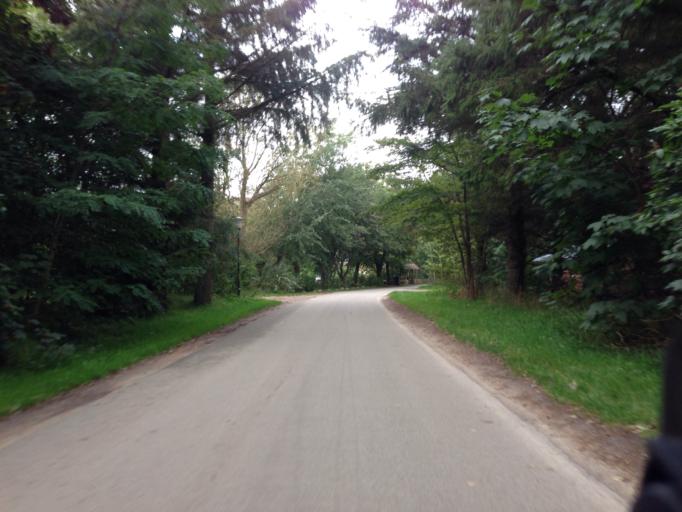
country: DE
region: Schleswig-Holstein
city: Nieblum
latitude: 54.6869
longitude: 8.4861
